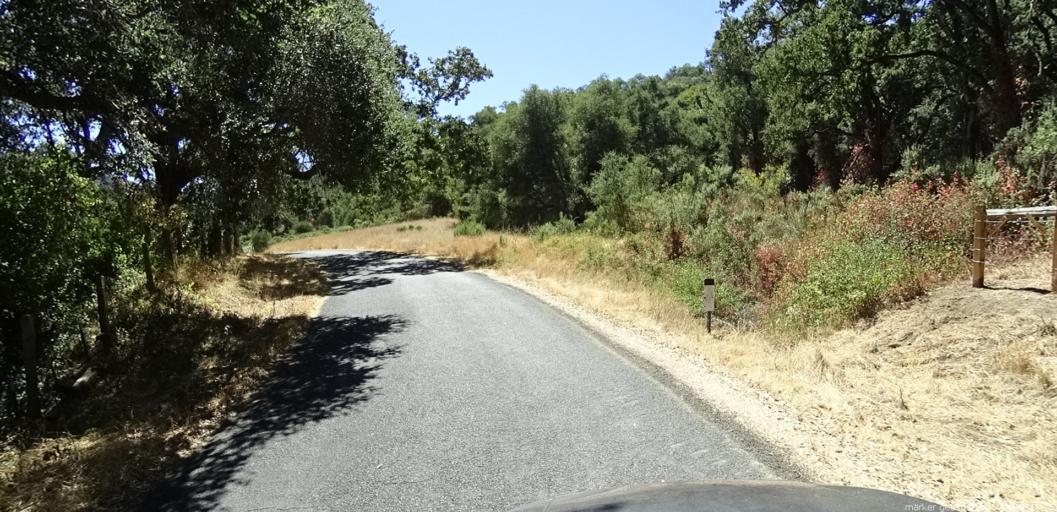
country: US
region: California
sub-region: Monterey County
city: Carmel Valley Village
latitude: 36.4377
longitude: -121.7946
